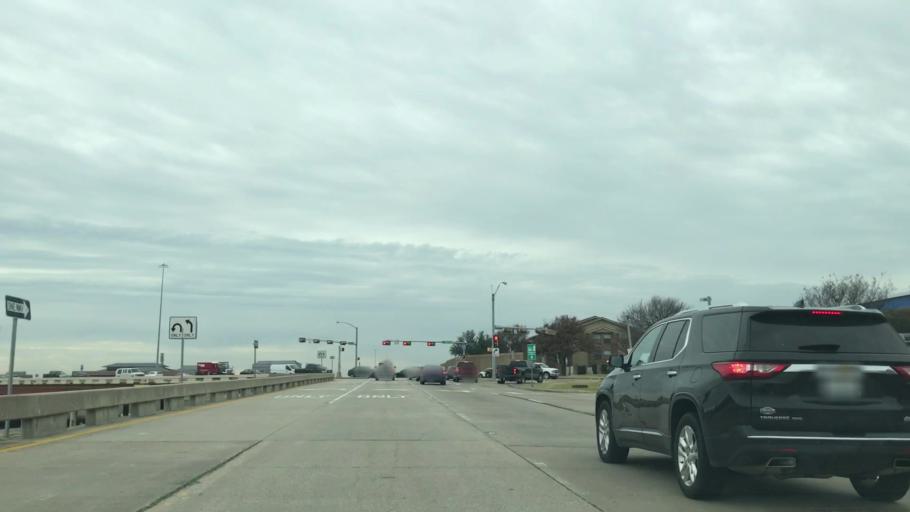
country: US
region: Texas
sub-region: Dallas County
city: Farmers Branch
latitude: 32.9058
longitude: -96.9575
